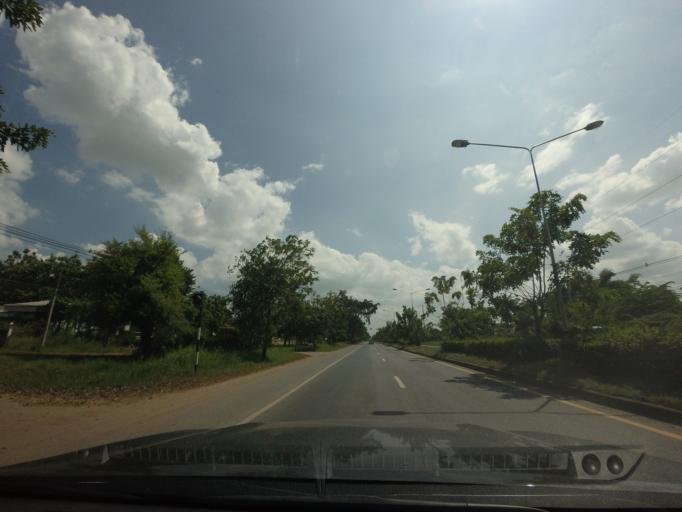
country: TH
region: Phetchabun
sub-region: Amphoe Bueng Sam Phan
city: Bueng Sam Phan
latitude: 15.8549
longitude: 101.0114
